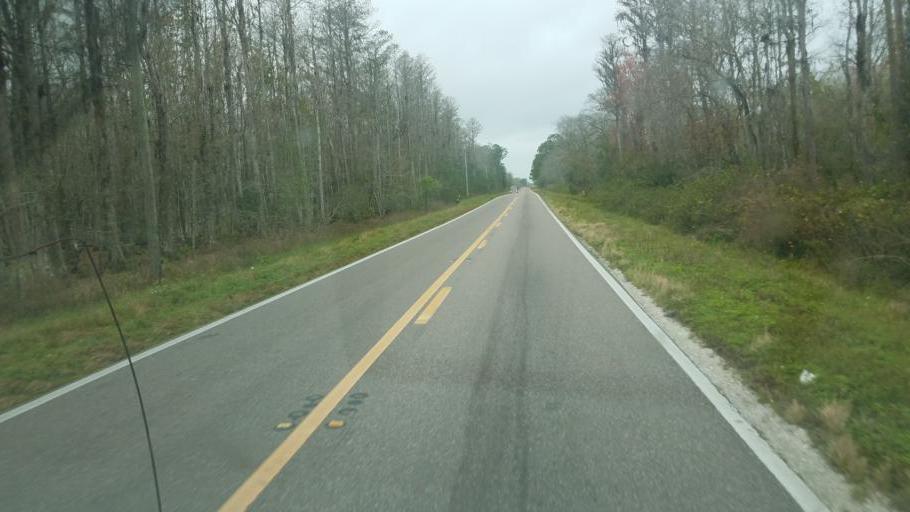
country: US
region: Florida
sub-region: Polk County
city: Polk City
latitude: 28.2584
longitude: -81.8295
